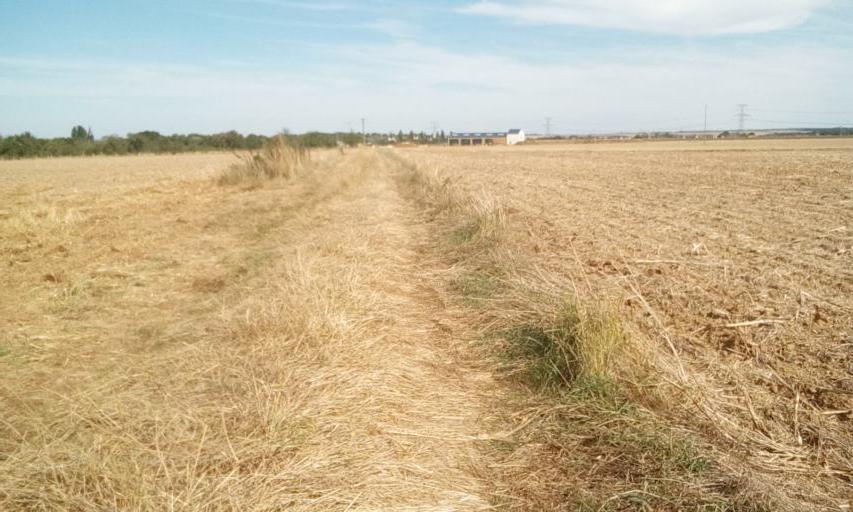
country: FR
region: Lower Normandy
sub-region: Departement du Calvados
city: Eterville
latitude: 49.1236
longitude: -0.4316
